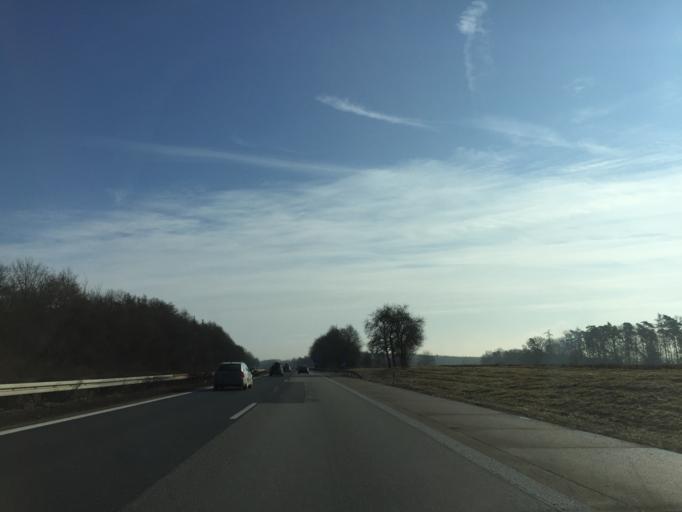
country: DE
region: Bavaria
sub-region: Regierungsbezirk Mittelfranken
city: Wachenroth
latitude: 49.7309
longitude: 10.7161
